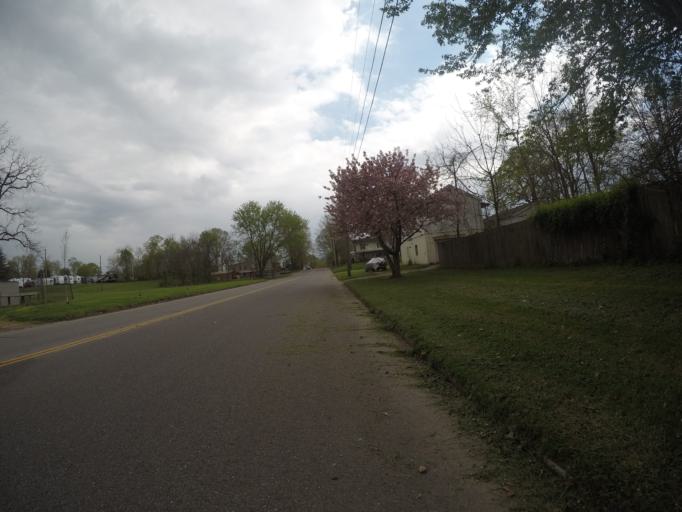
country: US
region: Ohio
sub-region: Washington County
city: Marietta
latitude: 39.4123
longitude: -81.4431
